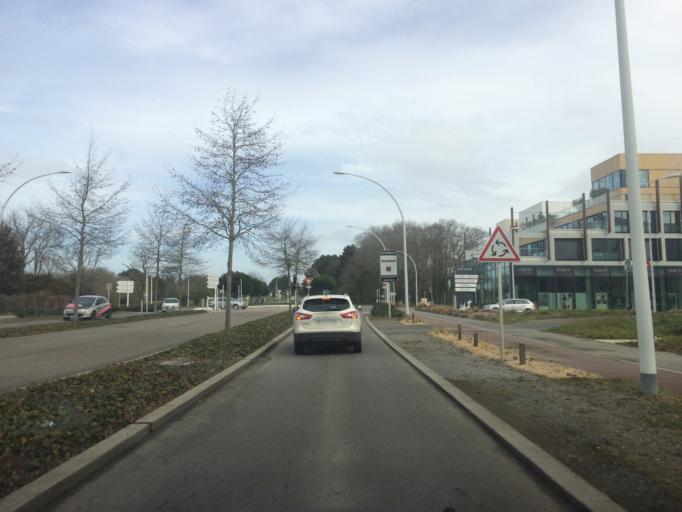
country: FR
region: Pays de la Loire
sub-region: Departement de la Loire-Atlantique
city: Saint-Nazaire
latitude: 47.2671
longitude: -2.2541
